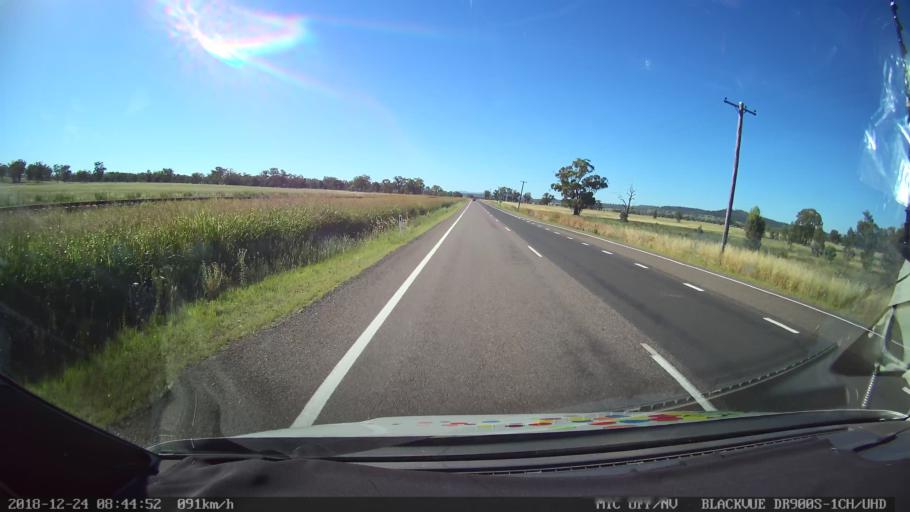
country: AU
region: New South Wales
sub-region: Liverpool Plains
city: Quirindi
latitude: -31.4074
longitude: 150.6499
